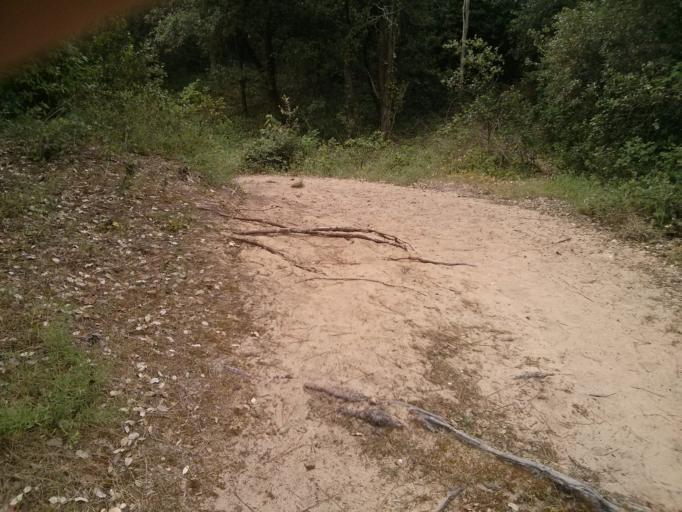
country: FR
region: Pays de la Loire
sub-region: Departement de la Vendee
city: Saint-Jean-de-Monts
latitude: 46.7926
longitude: -2.0727
